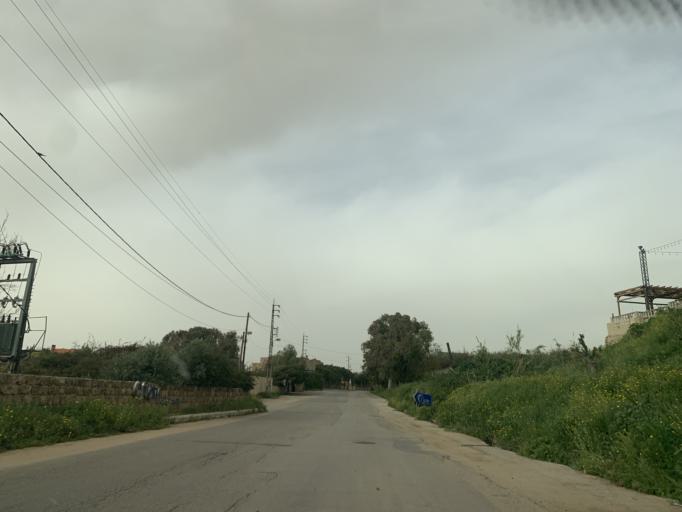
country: LB
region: Mont-Liban
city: Jbail
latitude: 34.1080
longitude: 35.6518
